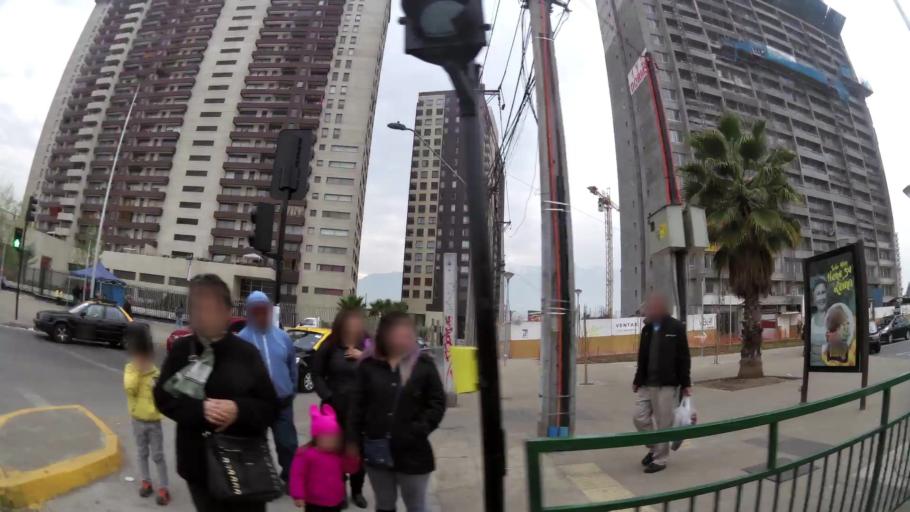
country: CL
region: Santiago Metropolitan
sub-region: Provincia de Santiago
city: Villa Presidente Frei, Nunoa, Santiago, Chile
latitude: -33.5211
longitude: -70.5990
